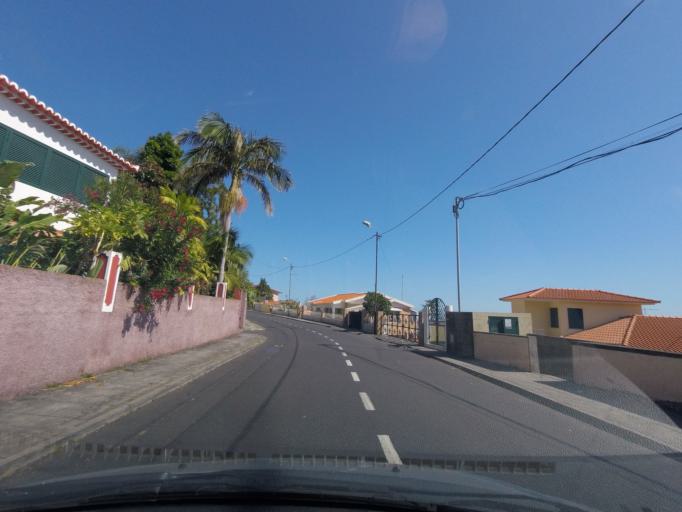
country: PT
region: Madeira
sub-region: Funchal
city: Nossa Senhora do Monte
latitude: 32.6579
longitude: -16.9083
